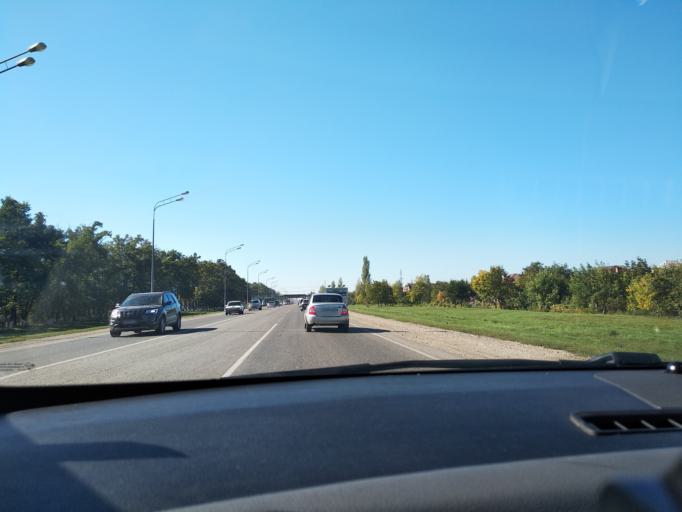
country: RU
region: Krasnodarskiy
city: Krasnodar
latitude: 45.1385
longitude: 39.0346
